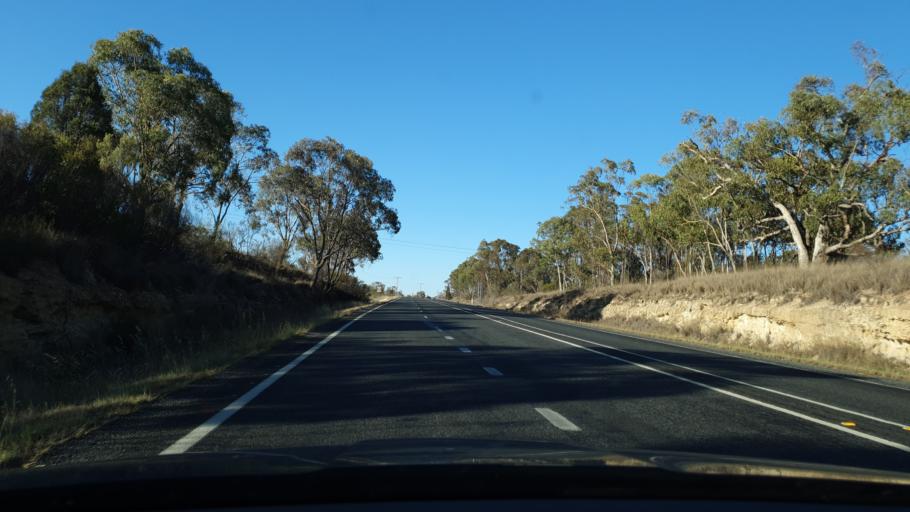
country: AU
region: Queensland
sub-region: Southern Downs
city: Stanthorpe
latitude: -28.6954
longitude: 151.9068
